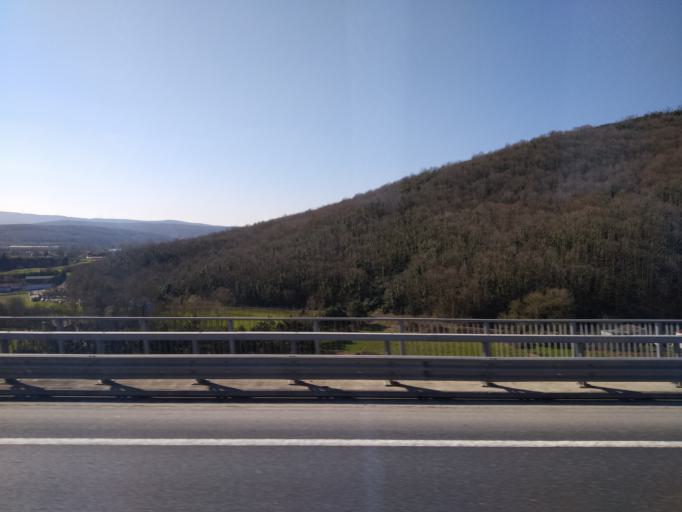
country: TR
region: Istanbul
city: Mahmut Sevket Pasa
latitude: 41.1370
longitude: 29.2863
